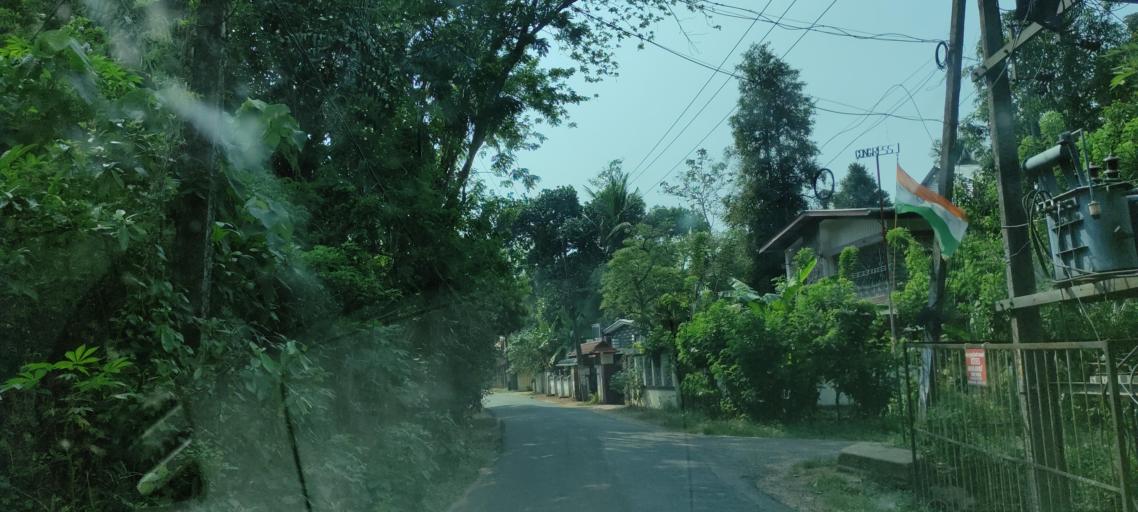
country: IN
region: Kerala
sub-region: Pattanamtitta
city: Tiruvalla
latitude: 9.3457
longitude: 76.5444
